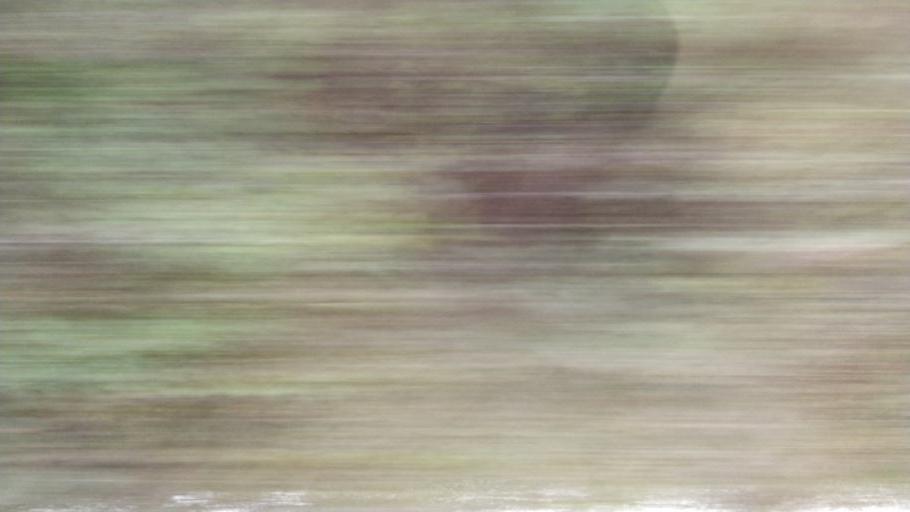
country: GB
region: England
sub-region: Borough of Bolton
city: Westhoughton
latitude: 53.5433
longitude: -2.5481
